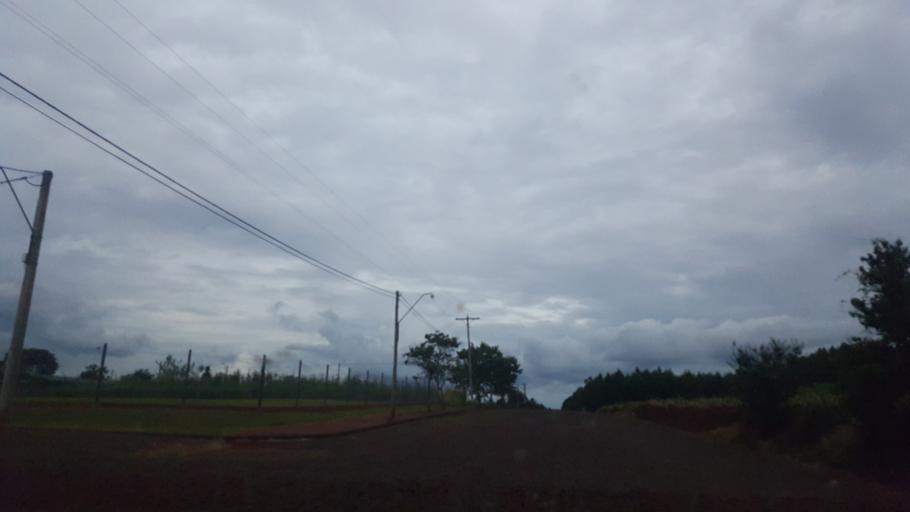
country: AR
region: Misiones
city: Capiovi
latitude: -26.9348
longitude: -55.0496
